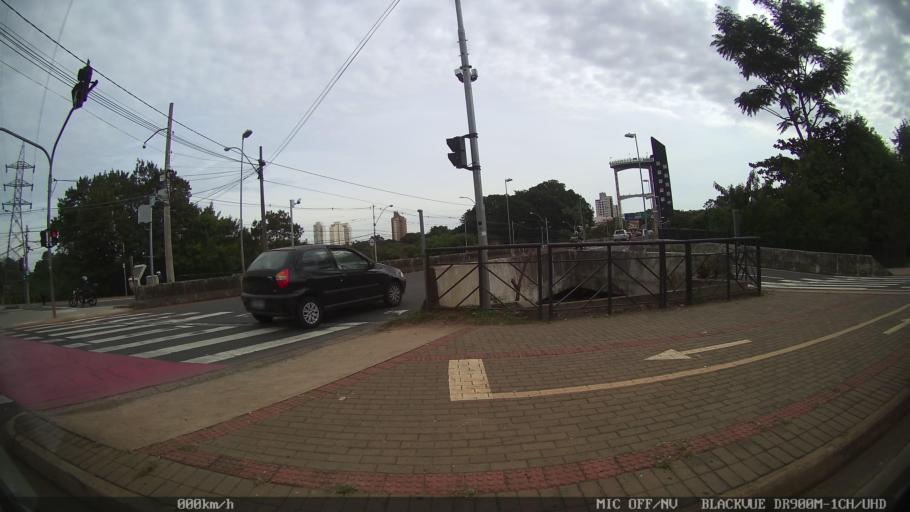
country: BR
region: Sao Paulo
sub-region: Piracicaba
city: Piracicaba
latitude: -22.7147
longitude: -47.6502
